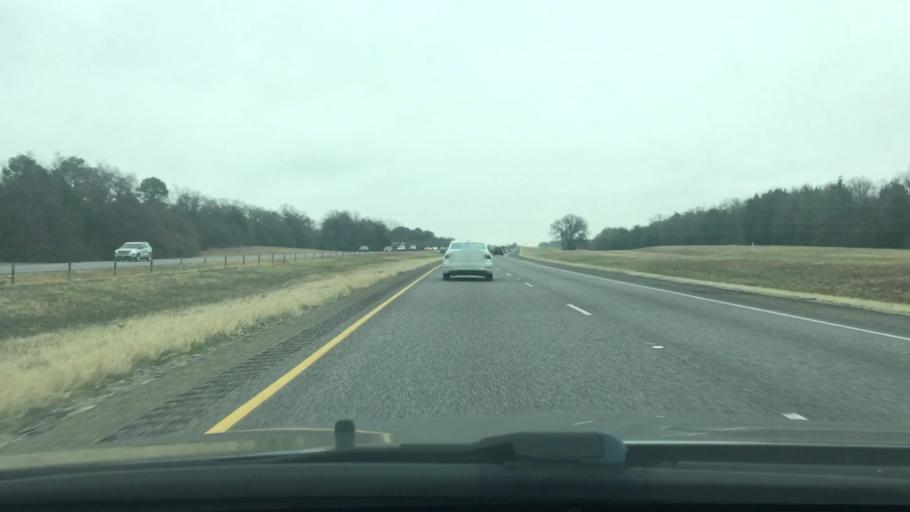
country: US
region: Texas
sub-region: Freestone County
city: Fairfield
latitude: 31.7790
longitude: -96.2305
